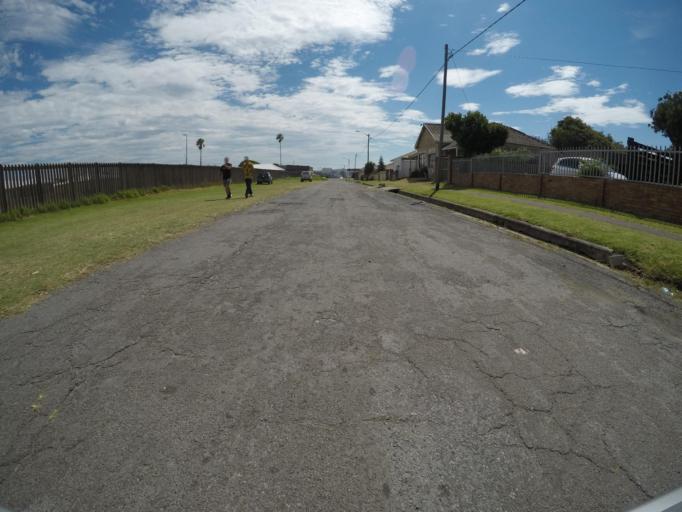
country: ZA
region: Eastern Cape
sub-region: Buffalo City Metropolitan Municipality
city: East London
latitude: -33.0315
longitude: 27.9075
